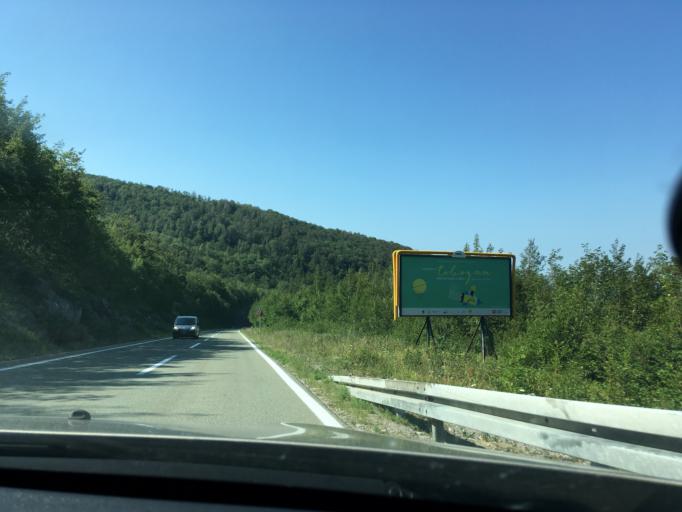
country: HR
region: Primorsko-Goranska
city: Hreljin
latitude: 45.3411
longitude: 14.6057
